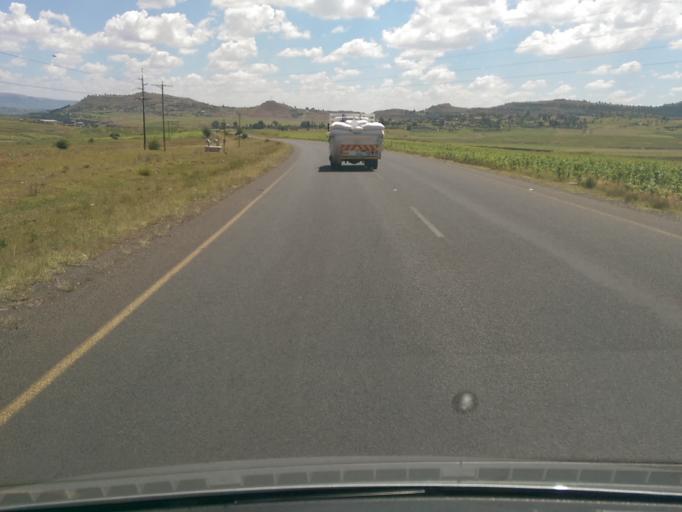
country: LS
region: Maseru
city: Maseru
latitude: -29.4200
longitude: 27.6600
